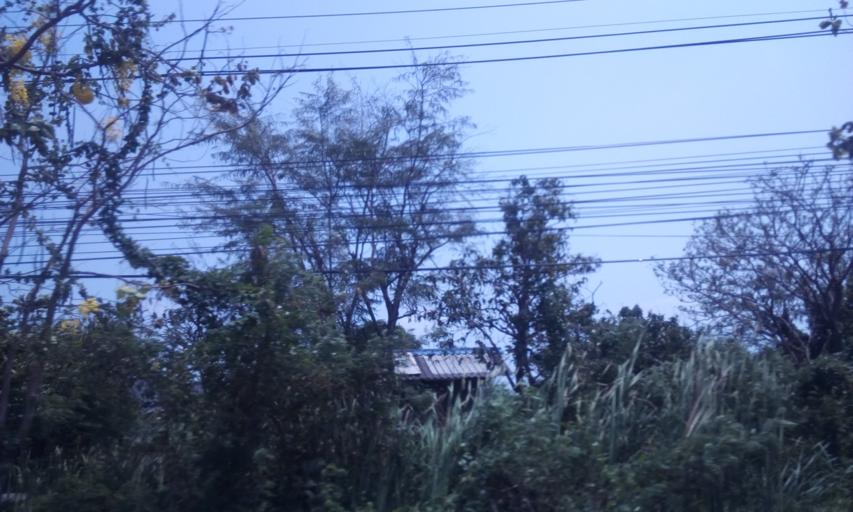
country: TH
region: Chachoengsao
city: Bang Nam Priao
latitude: 13.7961
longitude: 101.0528
